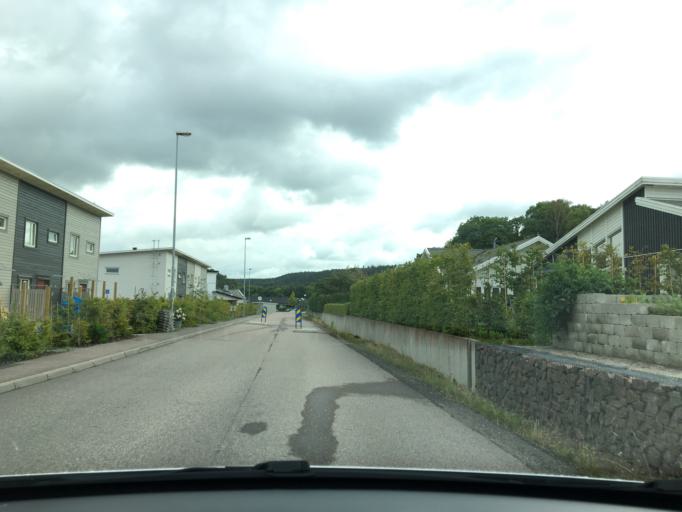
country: SE
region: Vaestra Goetaland
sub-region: Ale Kommun
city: Nodinge-Nol
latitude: 57.8874
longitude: 12.0586
